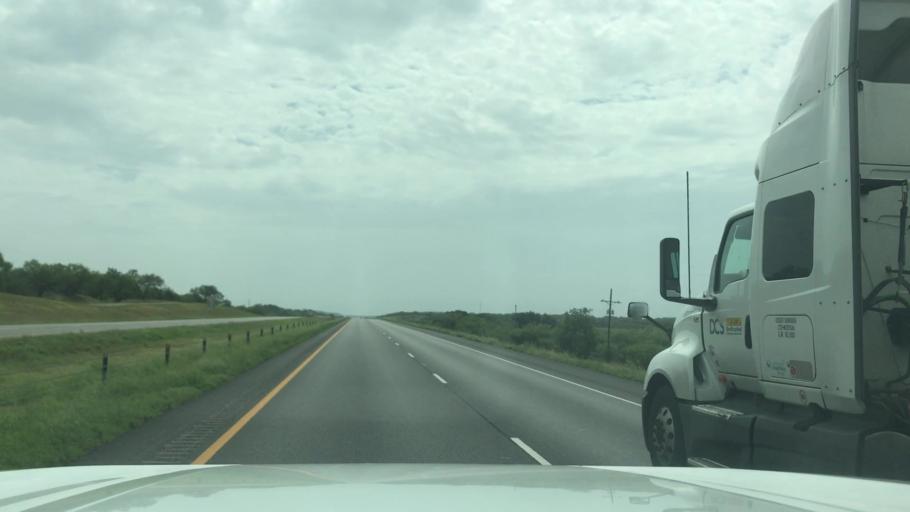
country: US
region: Texas
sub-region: Callahan County
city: Baird
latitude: 32.3829
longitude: -99.2811
